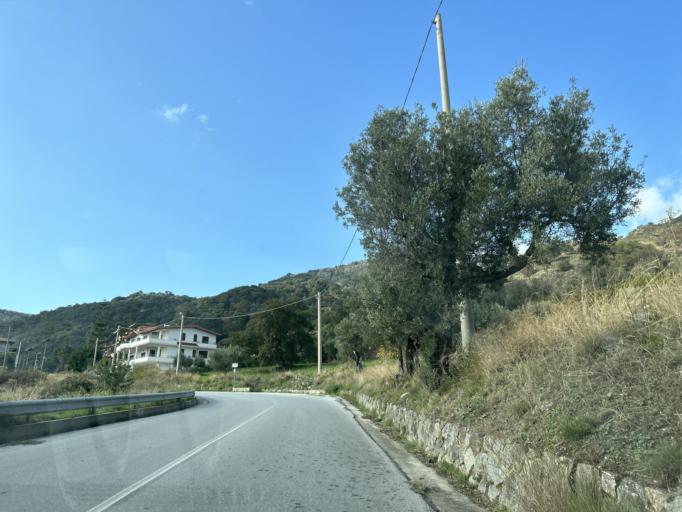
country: IT
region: Calabria
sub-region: Provincia di Catanzaro
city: Gasperina
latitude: 38.7272
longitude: 16.5175
